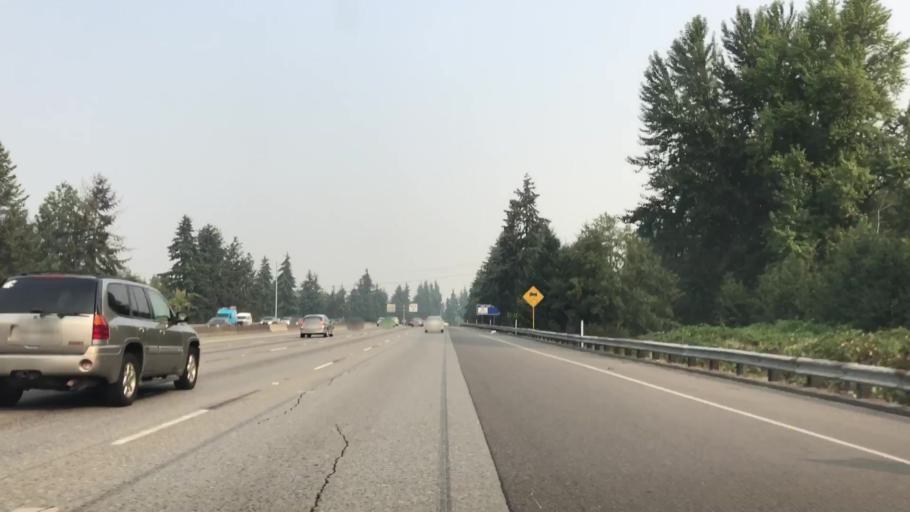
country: US
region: Washington
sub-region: King County
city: Shoreline
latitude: 47.7396
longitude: -122.3278
